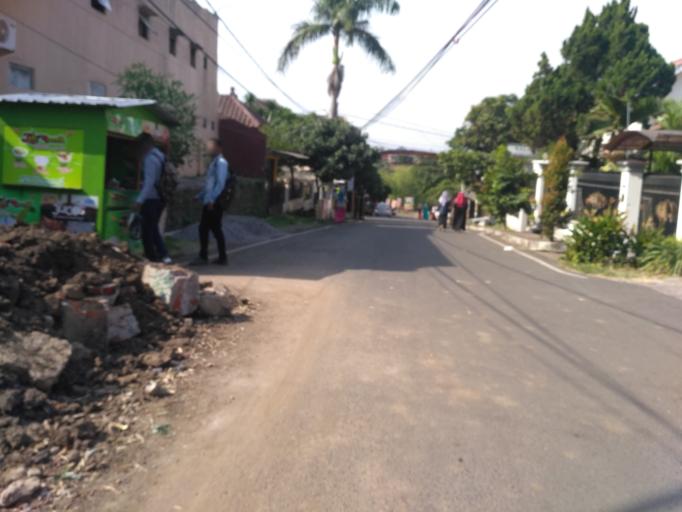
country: ID
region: East Java
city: Malang
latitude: -7.9352
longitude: 112.6075
